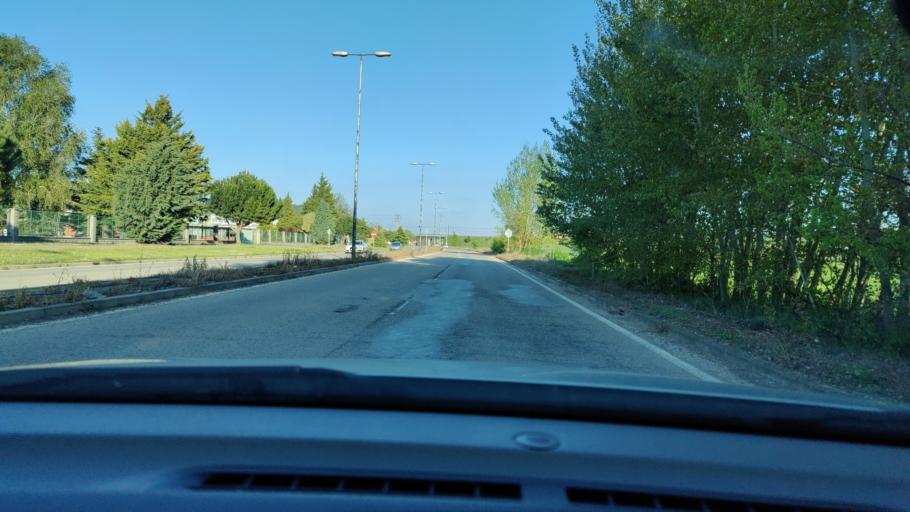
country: ES
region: Castille and Leon
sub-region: Provincia de Burgos
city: Villalbilla de Burgos
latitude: 42.3588
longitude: -3.7664
